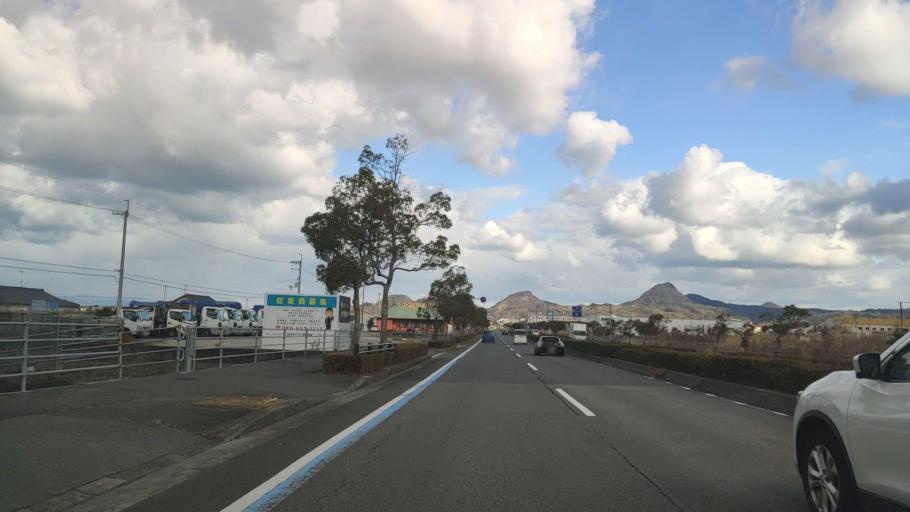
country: JP
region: Ehime
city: Hojo
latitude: 33.9567
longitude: 132.7762
